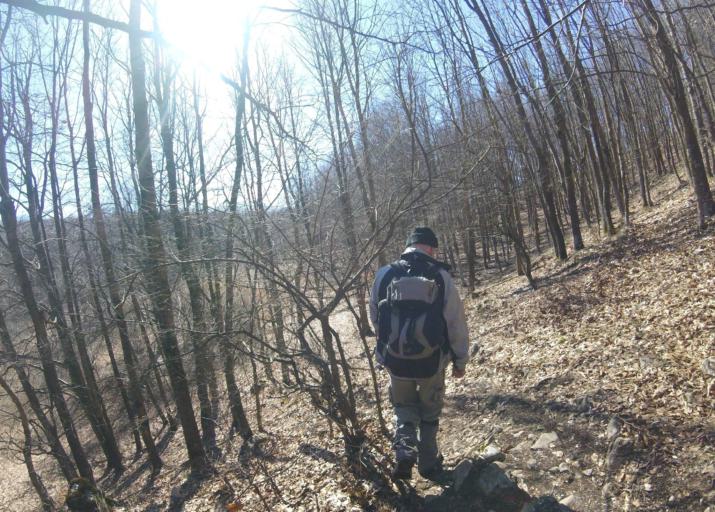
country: HU
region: Heves
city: Szilvasvarad
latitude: 48.0622
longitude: 20.4703
